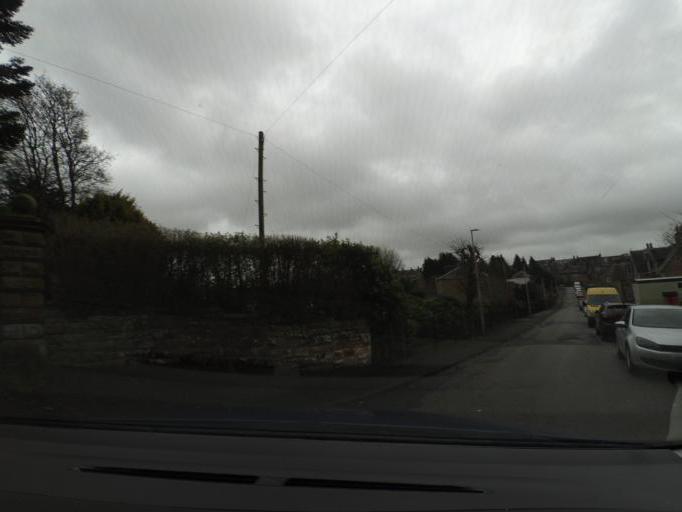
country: GB
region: Scotland
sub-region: The Scottish Borders
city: Hawick
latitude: 55.4315
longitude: -2.7863
